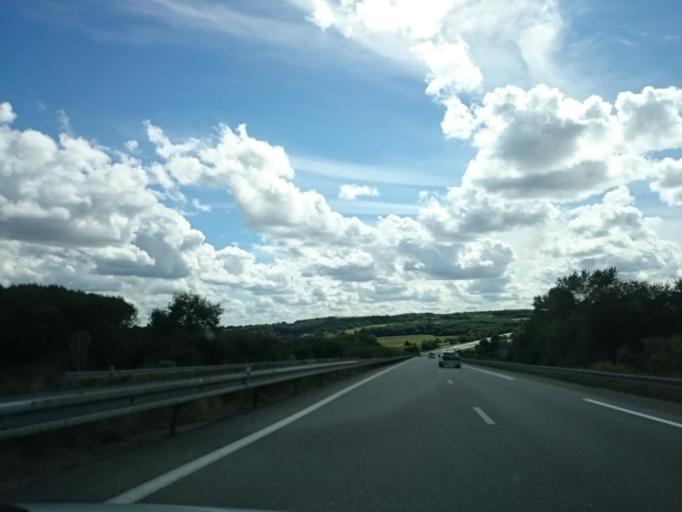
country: FR
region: Pays de la Loire
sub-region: Departement de la Loire-Atlantique
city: Mauves-sur-Loire
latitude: 47.3170
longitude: -1.4102
